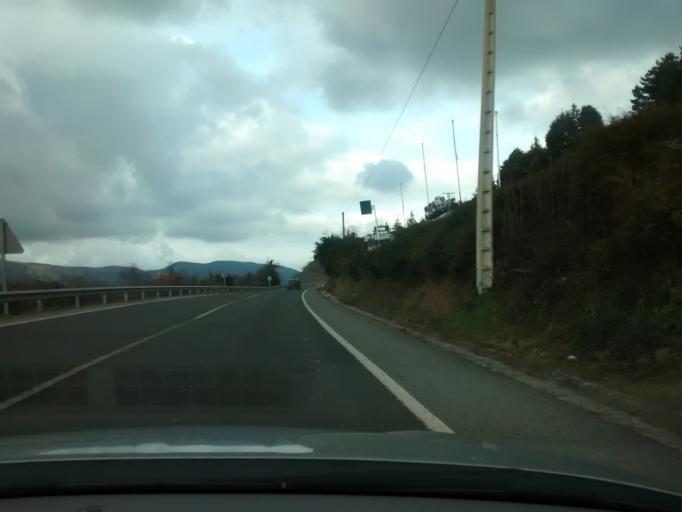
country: ES
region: Castille and Leon
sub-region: Provincia de Burgos
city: Villasana de Mena
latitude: 43.1533
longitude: -3.2639
